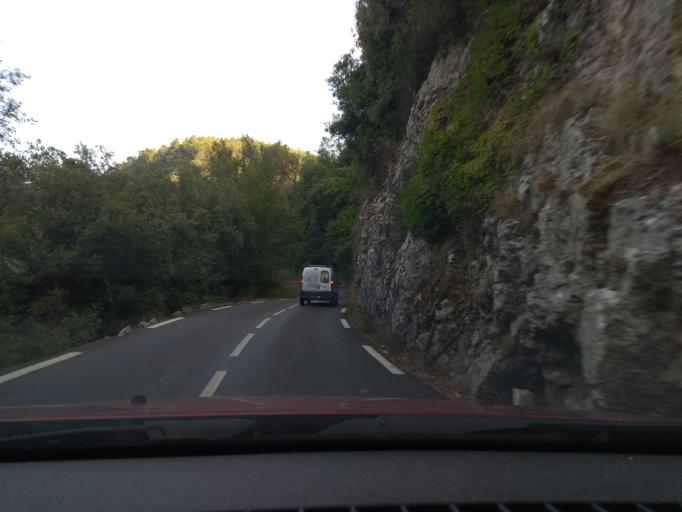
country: FR
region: Provence-Alpes-Cote d'Azur
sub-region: Departement des Alpes-Maritimes
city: La Colle-sur-Loup
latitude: 43.6860
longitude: 7.0712
